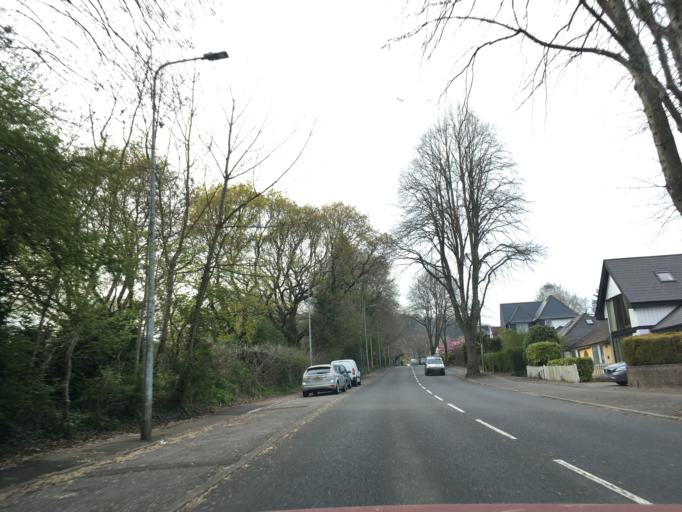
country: GB
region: Wales
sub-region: Cardiff
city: Radyr
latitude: 51.5292
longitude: -3.2214
